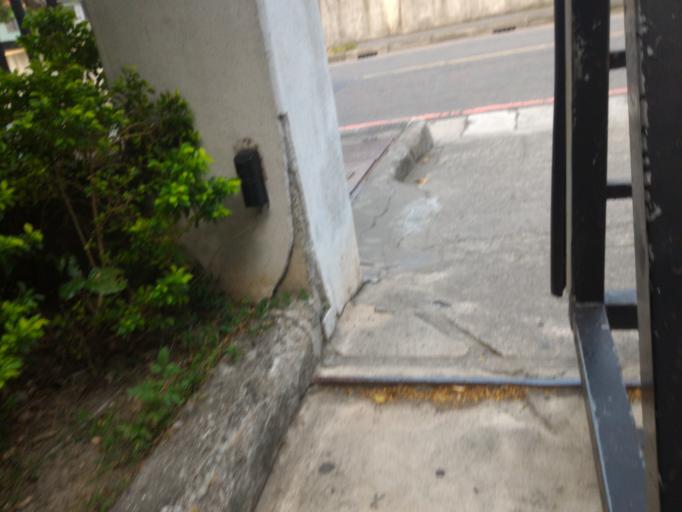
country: TW
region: Taipei
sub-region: Taipei
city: Banqiao
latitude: 25.0182
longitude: 121.4680
